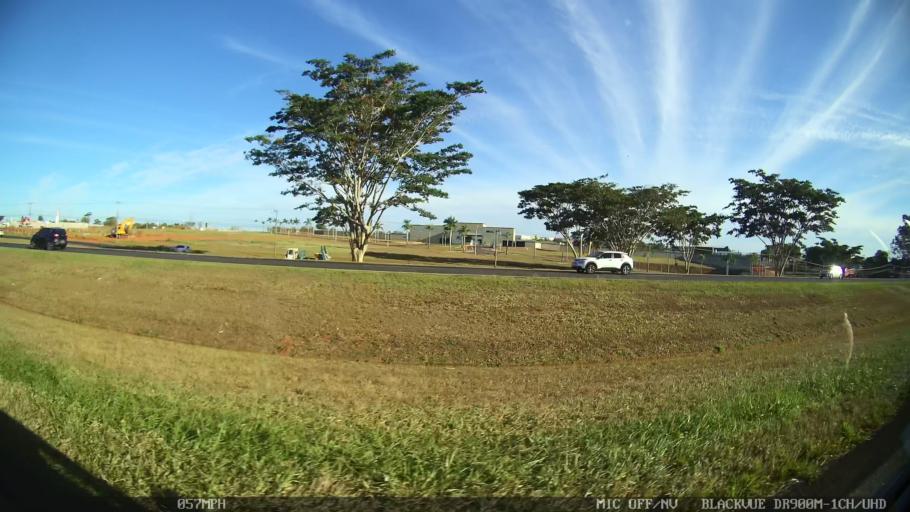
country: BR
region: Sao Paulo
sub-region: Sao Jose Do Rio Preto
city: Sao Jose do Rio Preto
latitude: -20.8232
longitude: -49.4179
